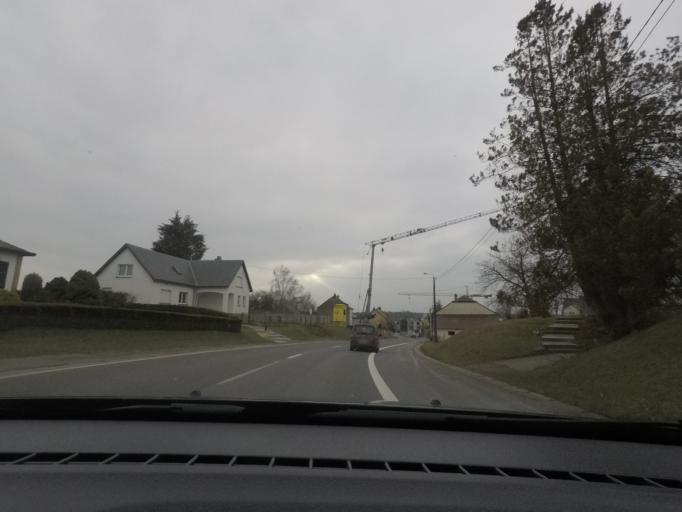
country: BE
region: Wallonia
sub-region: Province du Luxembourg
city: Etalle
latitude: 49.6769
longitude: 5.6043
